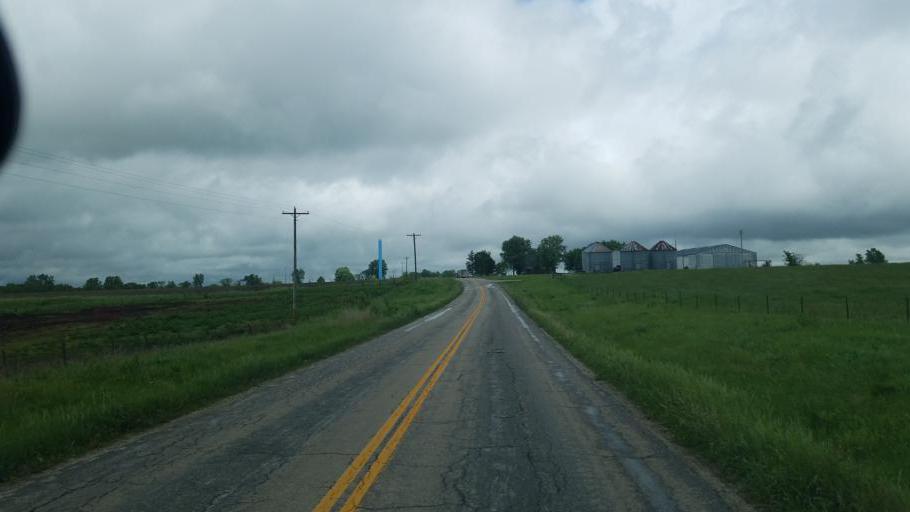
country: US
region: Missouri
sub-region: Mercer County
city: Princeton
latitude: 40.3718
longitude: -93.6803
